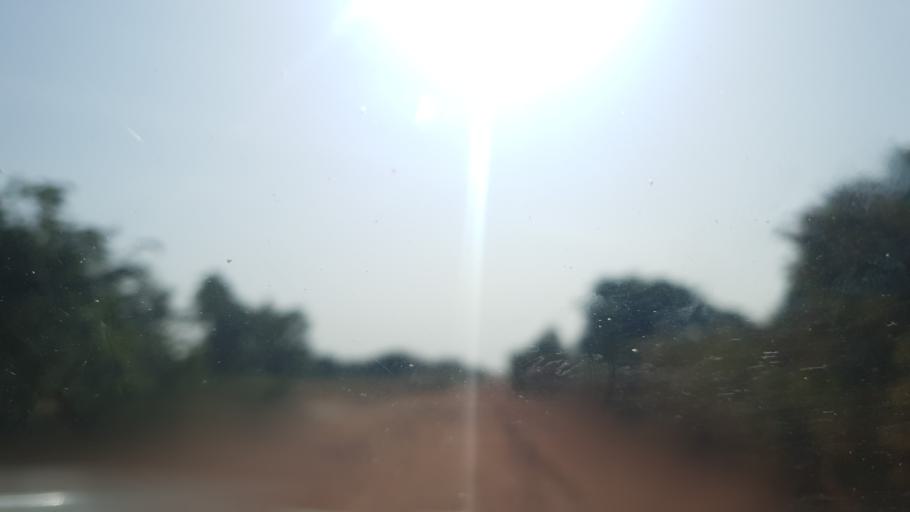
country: ML
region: Koulikoro
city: Dioila
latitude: 12.7034
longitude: -6.7667
